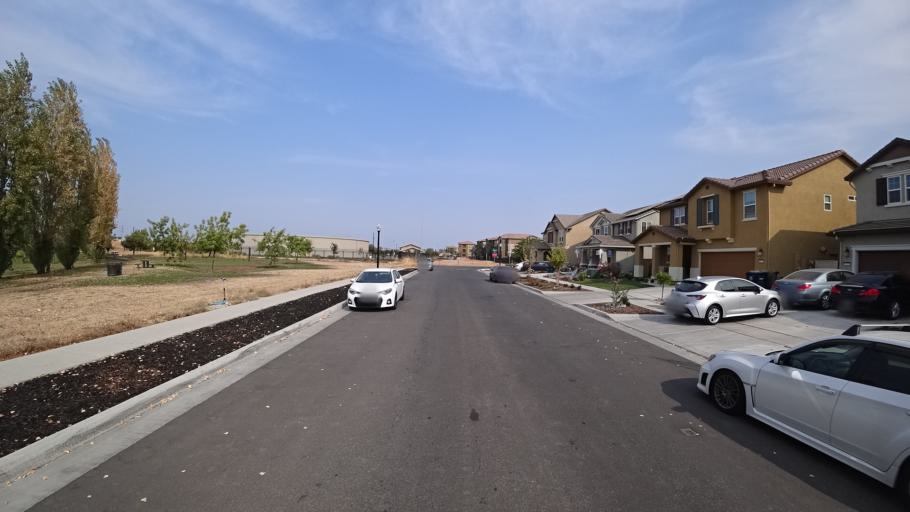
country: US
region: California
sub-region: Sacramento County
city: Laguna
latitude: 38.4519
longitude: -121.4136
